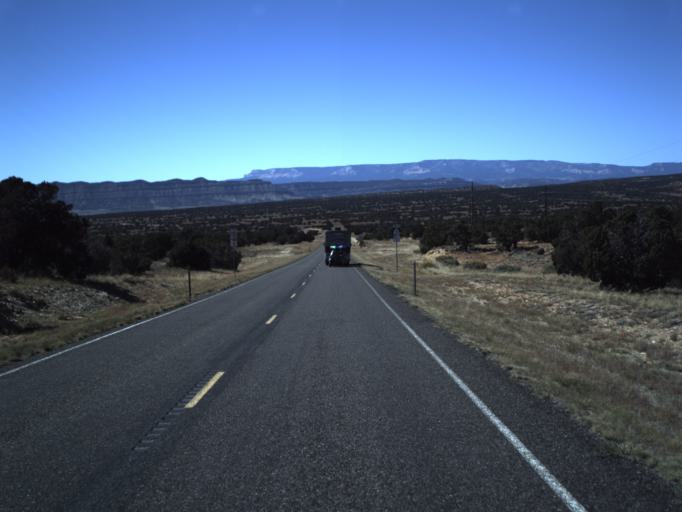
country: US
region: Utah
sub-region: Wayne County
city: Loa
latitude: 37.7499
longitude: -111.4770
